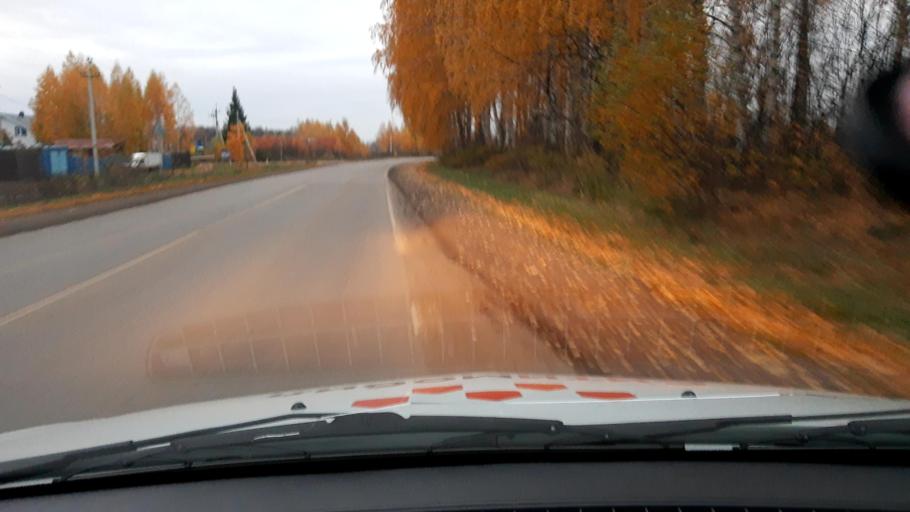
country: RU
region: Bashkortostan
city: Kabakovo
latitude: 54.7064
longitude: 56.1696
